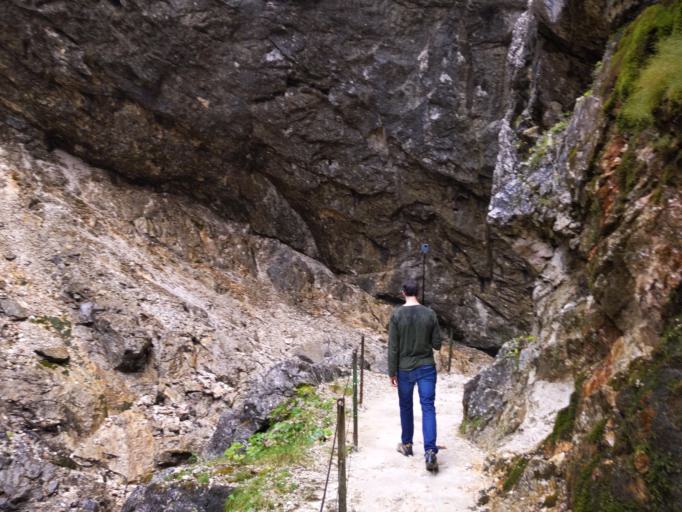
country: DE
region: Bavaria
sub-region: Upper Bavaria
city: Grainau
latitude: 47.4447
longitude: 11.0424
